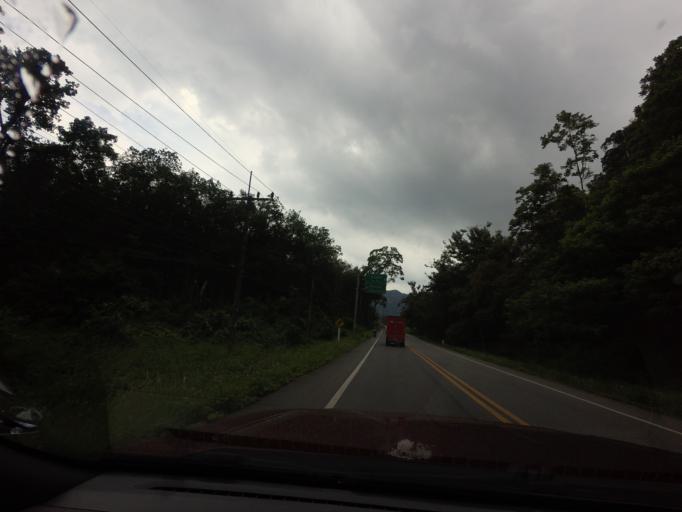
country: TH
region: Yala
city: Ban Nang Sata
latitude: 6.2360
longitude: 101.2159
